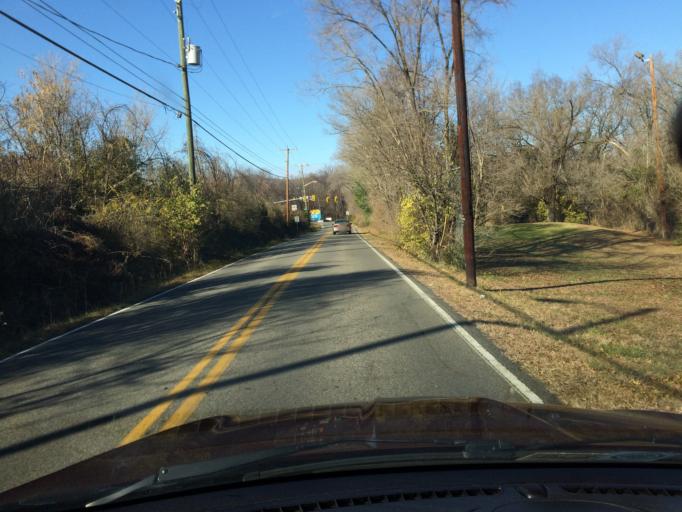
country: US
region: Virginia
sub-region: Roanoke County
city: Hollins
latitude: 37.3317
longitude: -79.9532
